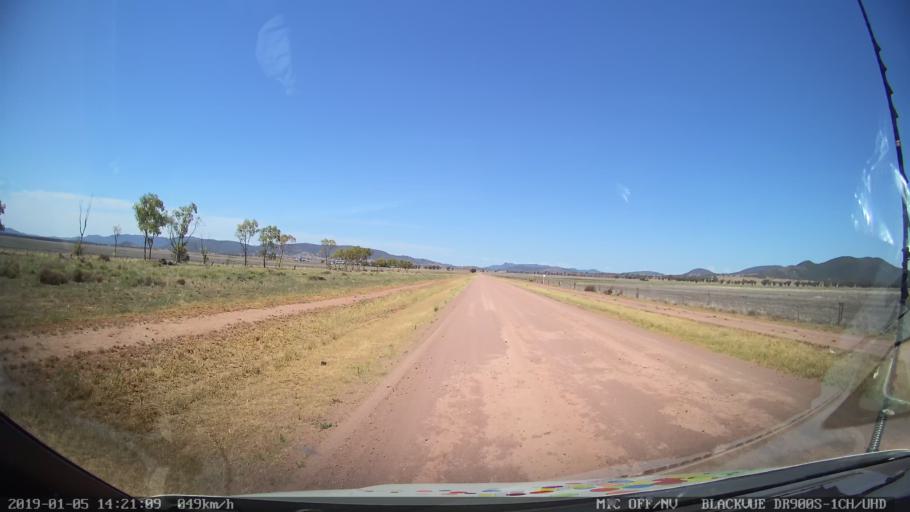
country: AU
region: New South Wales
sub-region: Liverpool Plains
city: Quirindi
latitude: -31.2469
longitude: 150.5110
